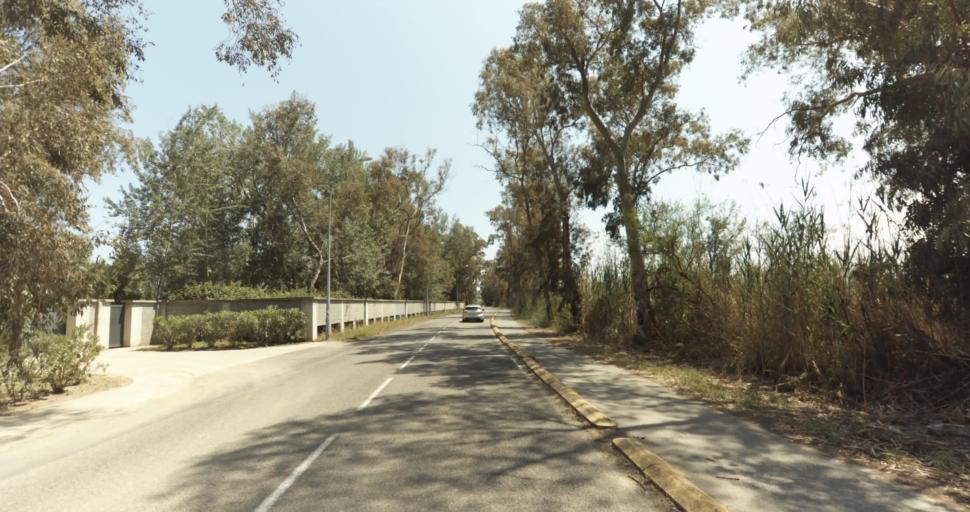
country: FR
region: Corsica
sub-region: Departement de la Haute-Corse
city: Biguglia
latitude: 42.6134
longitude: 9.4803
